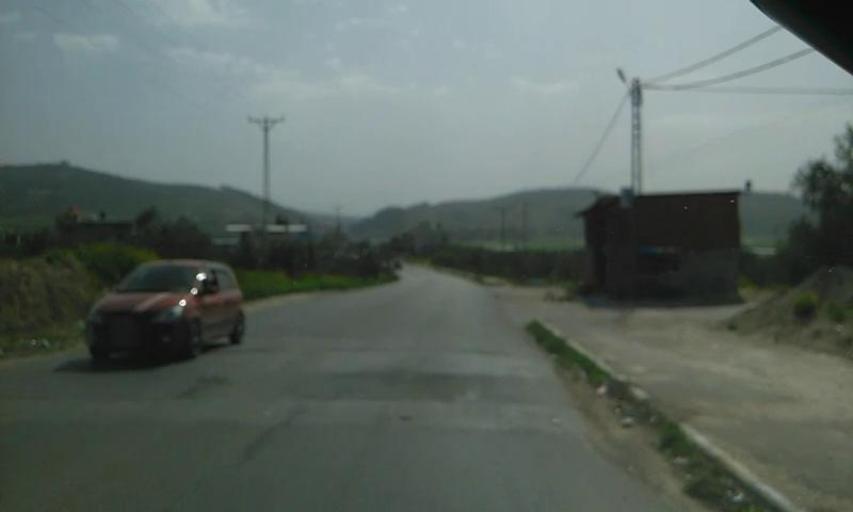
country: PS
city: Bir al Basha
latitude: 32.4187
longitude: 35.2301
